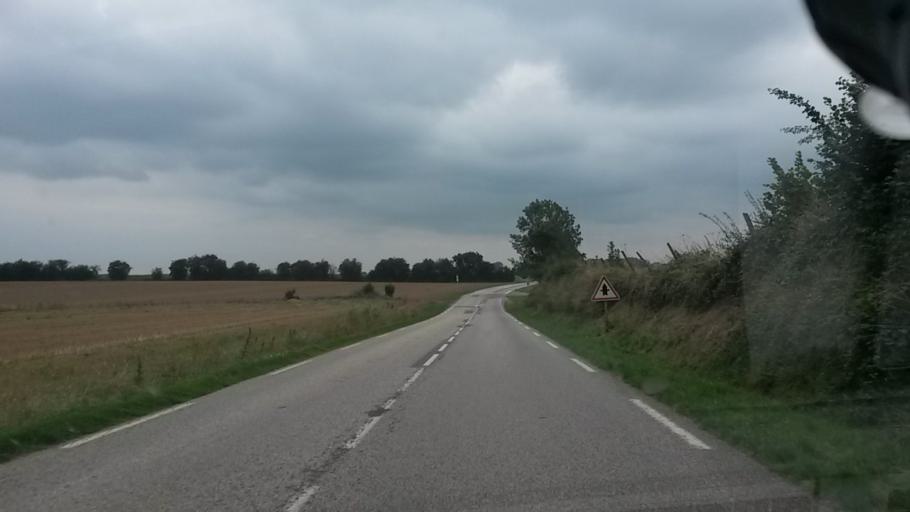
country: FR
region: Haute-Normandie
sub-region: Departement de la Seine-Maritime
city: Gaillefontaine
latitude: 49.6843
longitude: 1.6309
